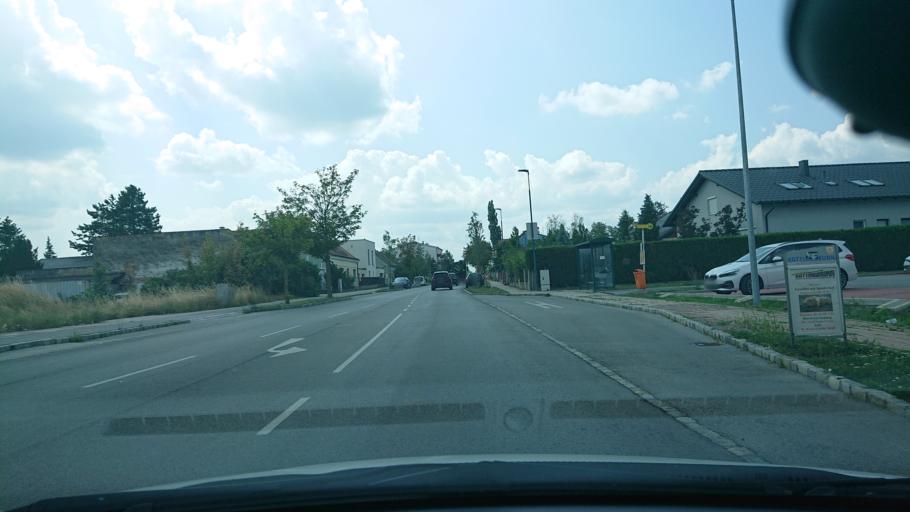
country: AT
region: Lower Austria
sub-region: Politischer Bezirk Baden
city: Kottingbrunn
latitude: 47.9461
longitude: 16.2226
